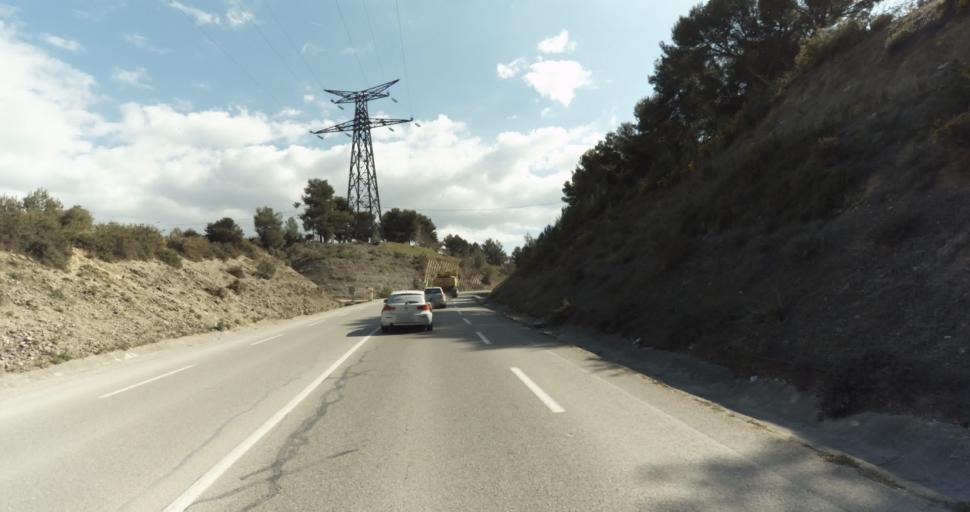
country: FR
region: Provence-Alpes-Cote d'Azur
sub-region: Departement des Bouches-du-Rhone
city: Gardanne
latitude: 43.4561
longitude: 5.4929
